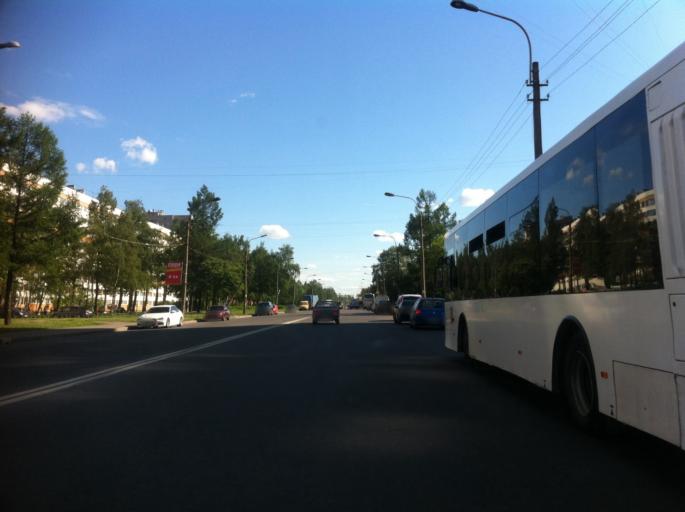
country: RU
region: St.-Petersburg
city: Uritsk
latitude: 59.8327
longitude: 30.1756
